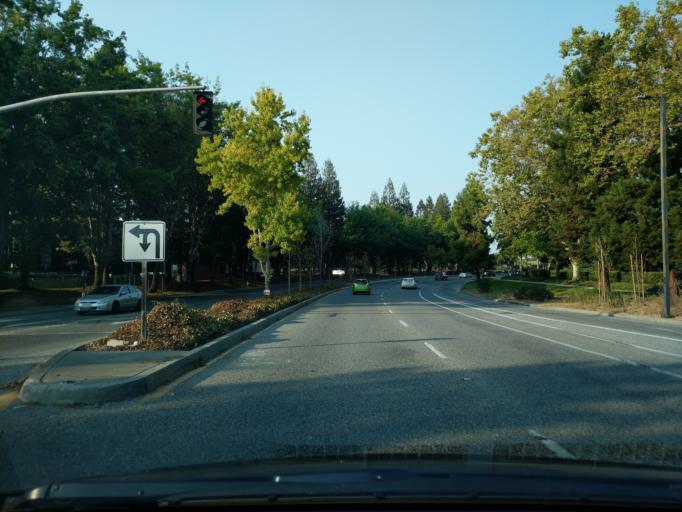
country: US
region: California
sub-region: Santa Clara County
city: Mountain View
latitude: 37.4225
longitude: -122.0916
